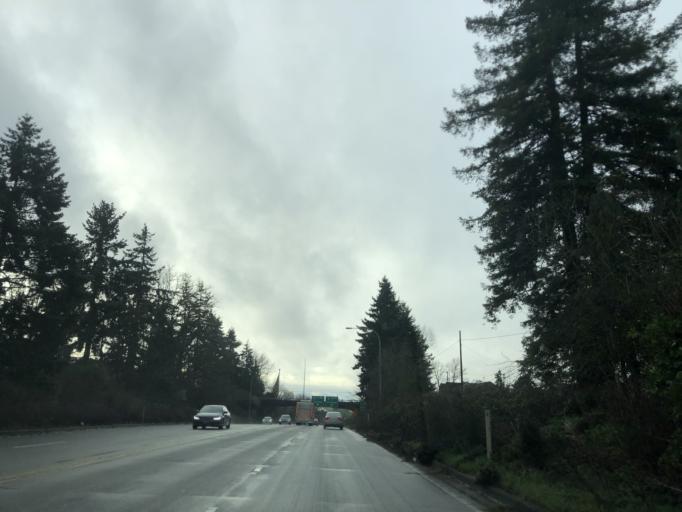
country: US
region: Washington
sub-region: Pierce County
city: Tacoma
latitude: 47.2384
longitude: -122.4633
